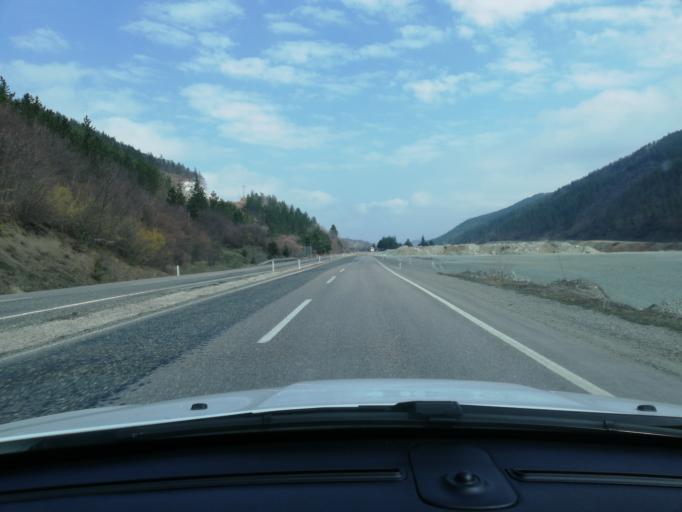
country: TR
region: Kastamonu
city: Kuzyaka
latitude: 41.1913
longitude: 33.7948
